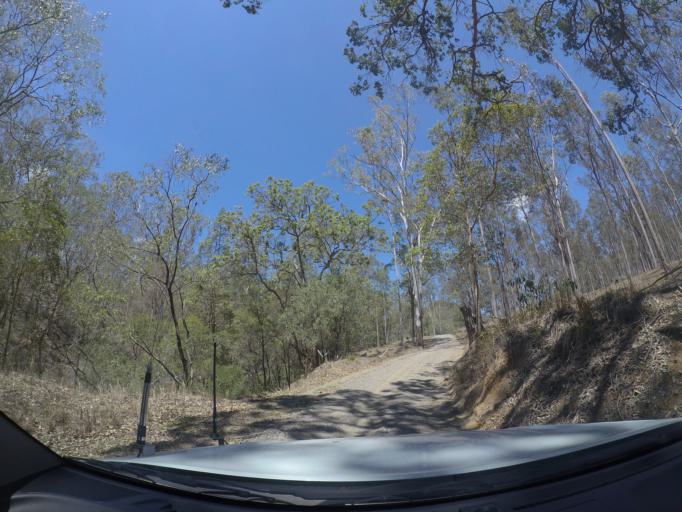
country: AU
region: Queensland
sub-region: Ipswich
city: Deebing Heights
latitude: -27.7663
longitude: 152.8112
